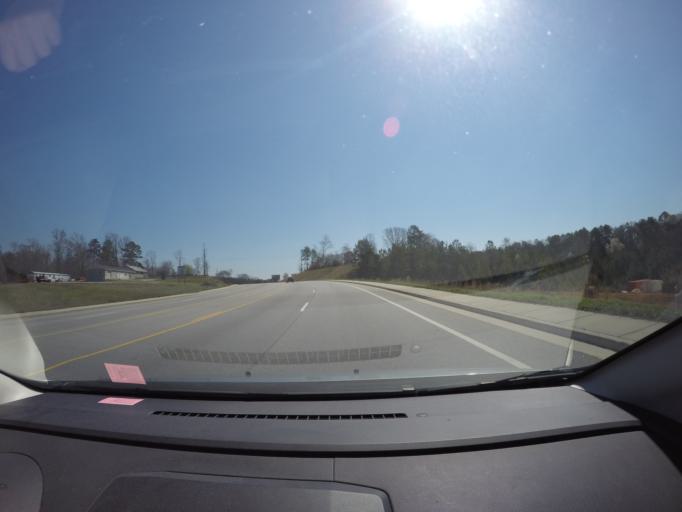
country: US
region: Tennessee
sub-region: Hamilton County
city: Harrison
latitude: 35.0708
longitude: -85.1055
